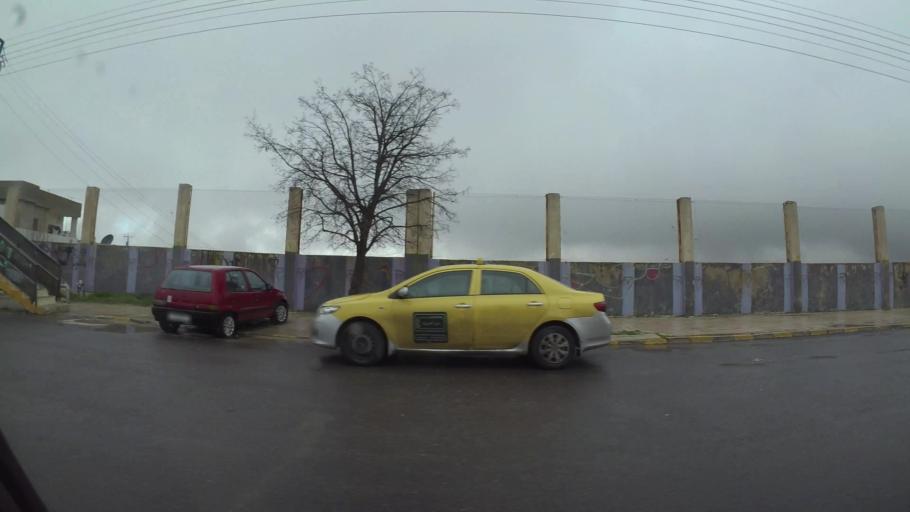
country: JO
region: Amman
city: Al Jubayhah
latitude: 32.0200
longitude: 35.8409
